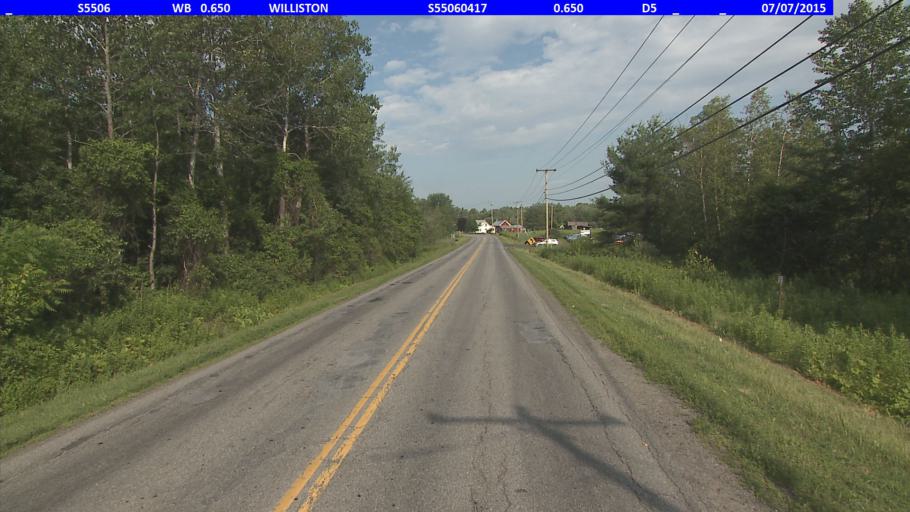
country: US
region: Vermont
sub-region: Chittenden County
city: Essex Junction
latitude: 44.4645
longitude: -73.1006
